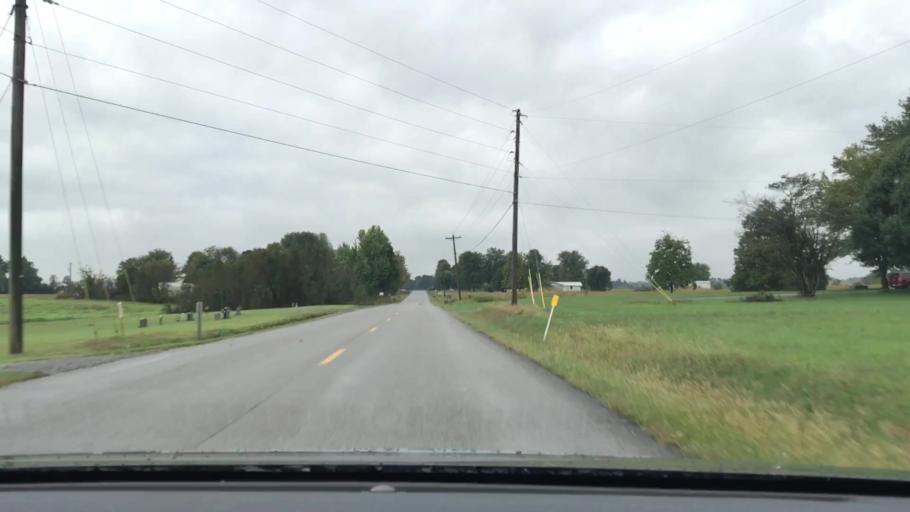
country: US
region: Kentucky
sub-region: McLean County
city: Calhoun
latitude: 37.4417
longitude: -87.2459
